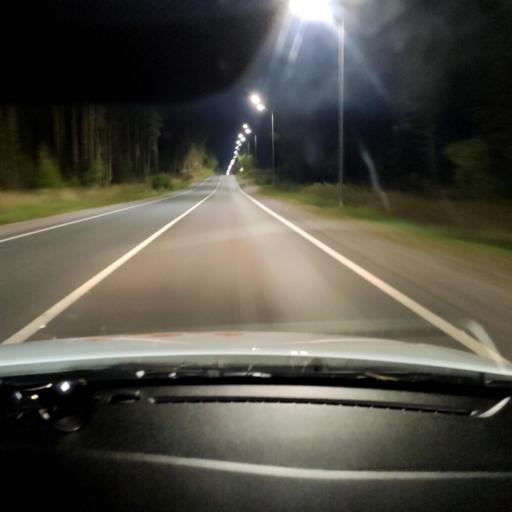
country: RU
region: Tatarstan
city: Verkhniy Uslon
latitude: 55.6383
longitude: 49.0436
